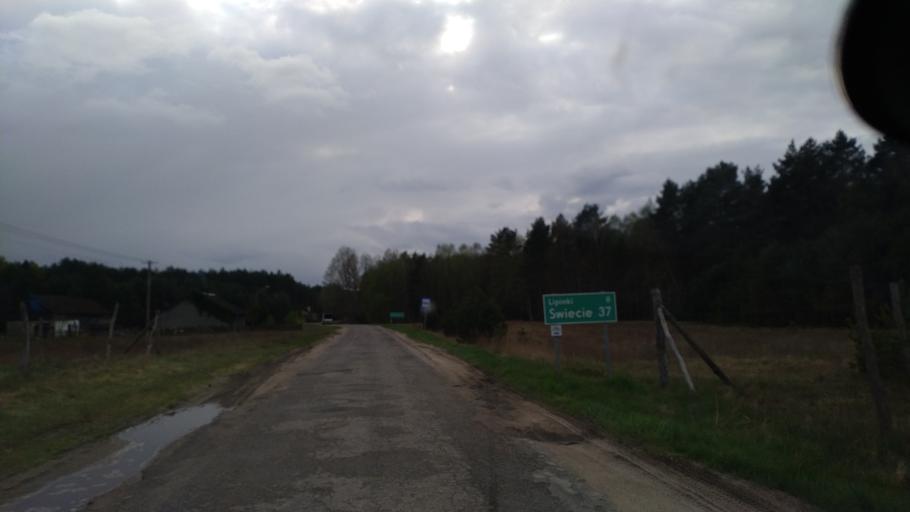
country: PL
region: Pomeranian Voivodeship
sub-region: Powiat starogardzki
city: Osiek
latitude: 53.6900
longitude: 18.5217
